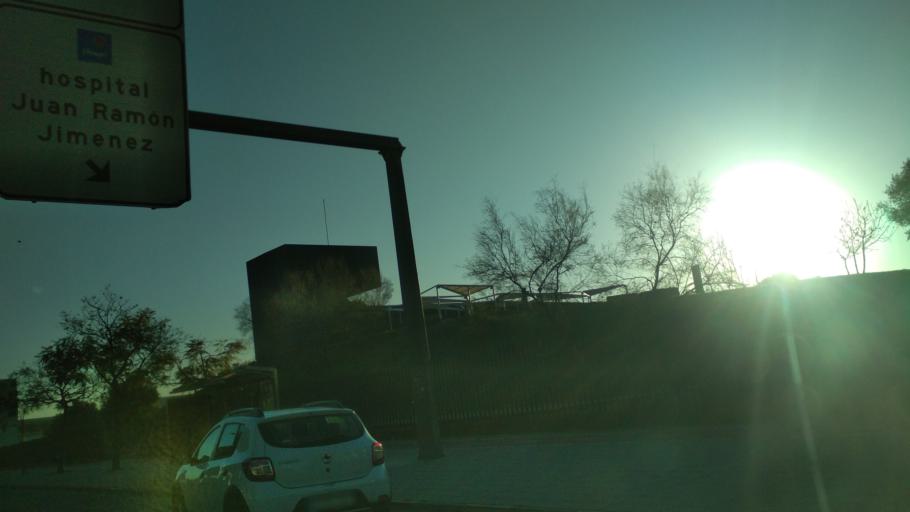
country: ES
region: Andalusia
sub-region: Provincia de Huelva
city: Huelva
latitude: 37.2726
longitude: -6.9282
